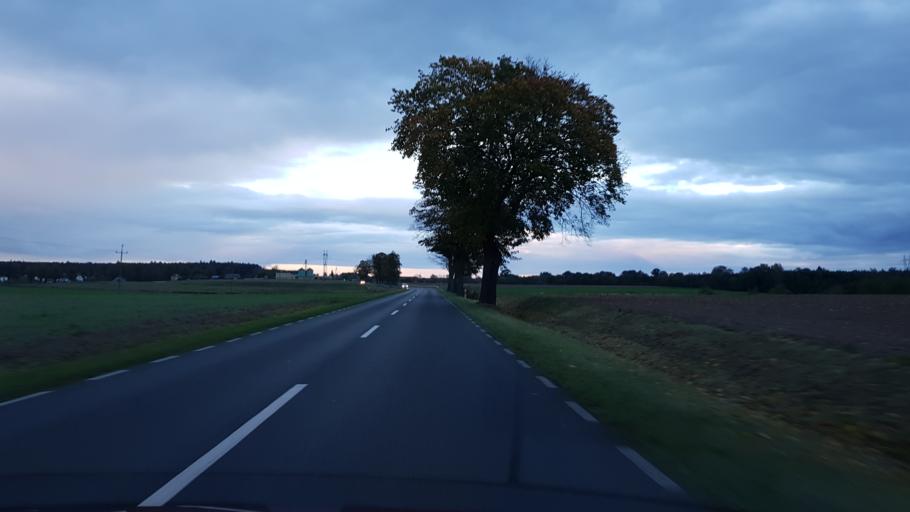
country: PL
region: Greater Poland Voivodeship
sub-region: Powiat zlotowski
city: Krajenka
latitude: 53.2581
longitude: 16.9108
